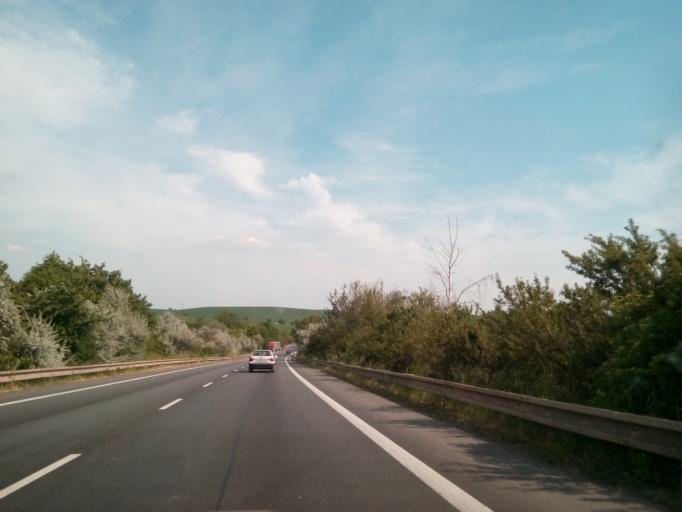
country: CZ
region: South Moravian
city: Krenovice
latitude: 49.1761
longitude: 16.8228
